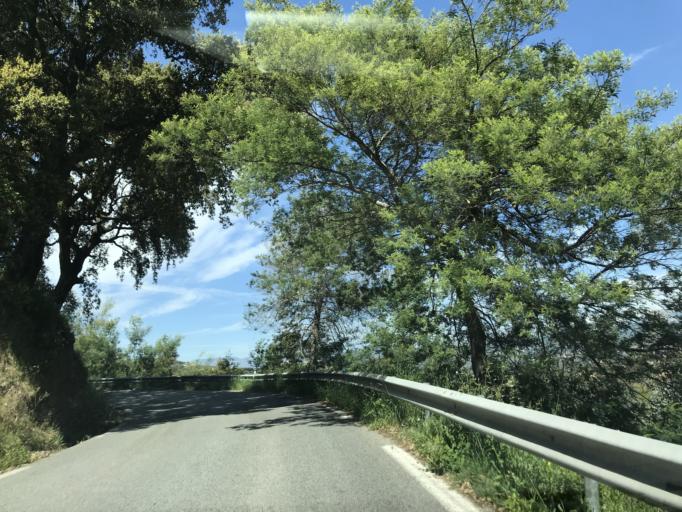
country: FR
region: Provence-Alpes-Cote d'Azur
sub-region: Departement des Alpes-Maritimes
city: Auribeau-sur-Siagne
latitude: 43.5853
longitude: 6.8967
